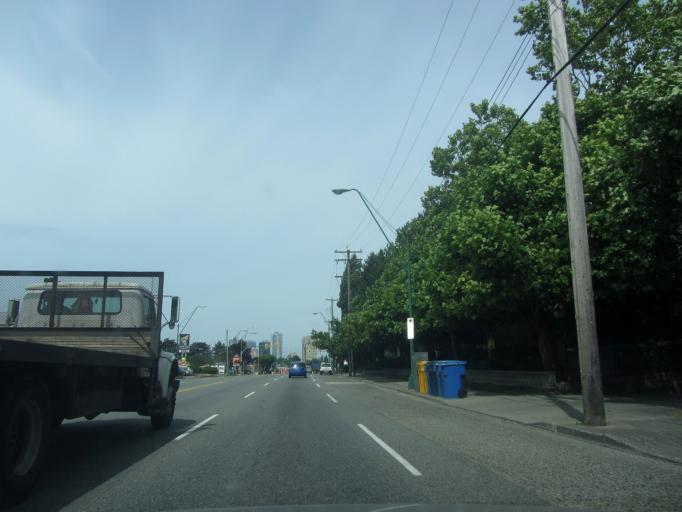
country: CA
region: British Columbia
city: New Westminster
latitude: 49.2185
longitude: -122.9566
